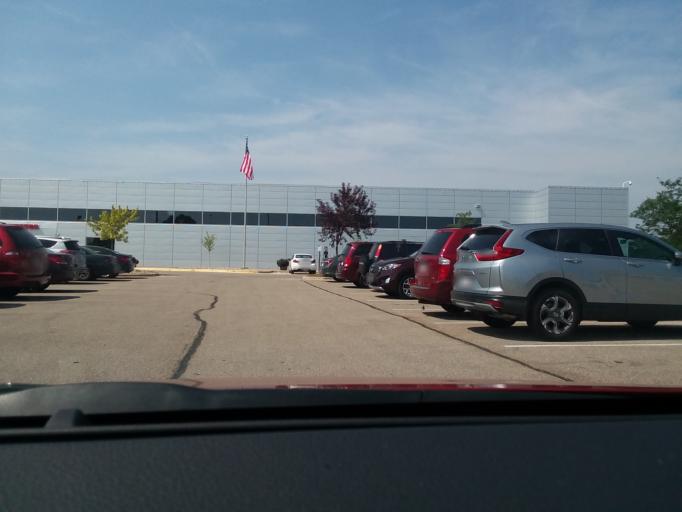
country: US
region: Wisconsin
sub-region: Dane County
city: Monona
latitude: 43.1223
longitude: -89.3089
